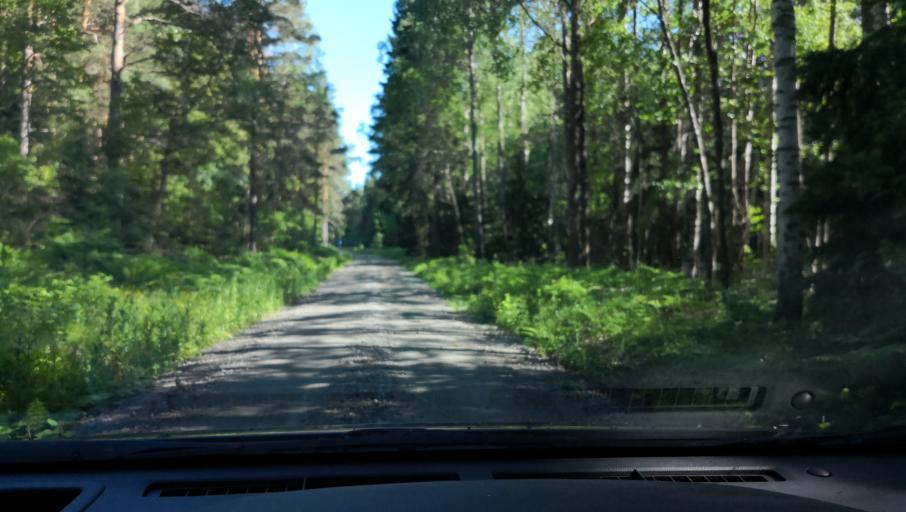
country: SE
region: Soedermanland
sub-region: Eskilstuna Kommun
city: Eskilstuna
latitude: 59.3349
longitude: 16.5745
